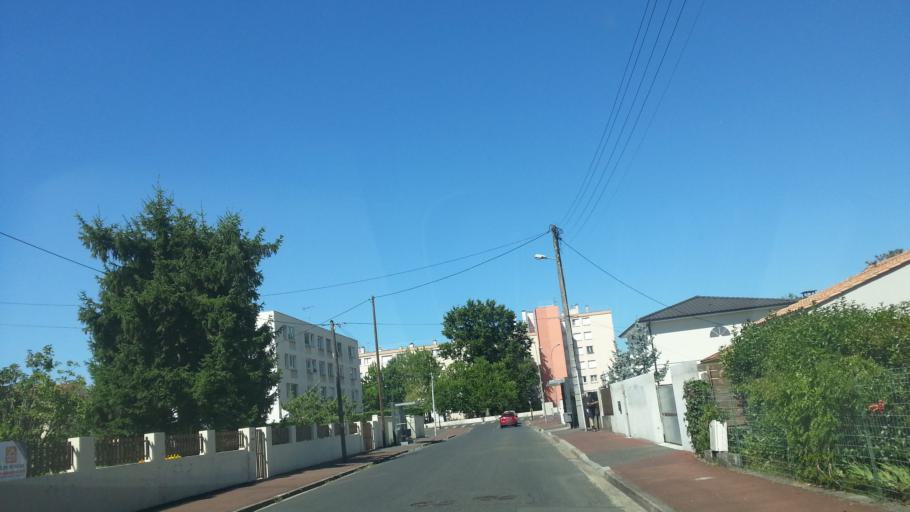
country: FR
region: Aquitaine
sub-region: Departement de la Gironde
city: Villenave-d'Ornon
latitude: 44.7640
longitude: -0.5644
